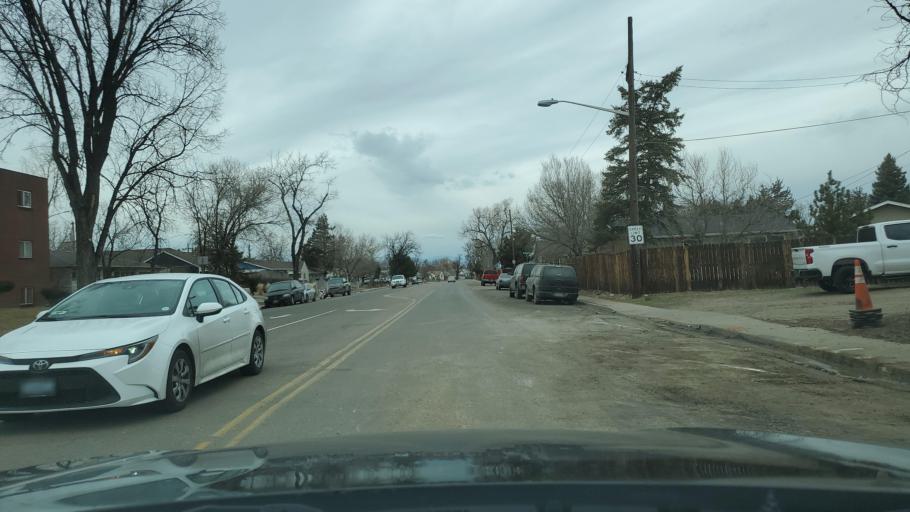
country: US
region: Colorado
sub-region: Adams County
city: Aurora
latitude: 39.7270
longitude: -104.8505
